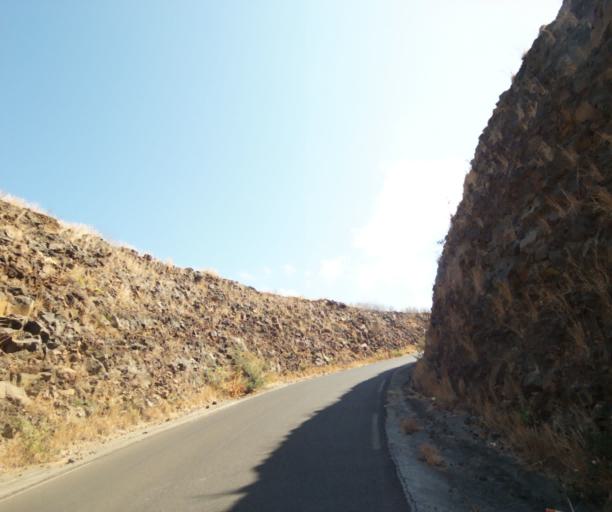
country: RE
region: Reunion
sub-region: Reunion
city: Trois-Bassins
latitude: -21.1024
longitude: 55.2502
